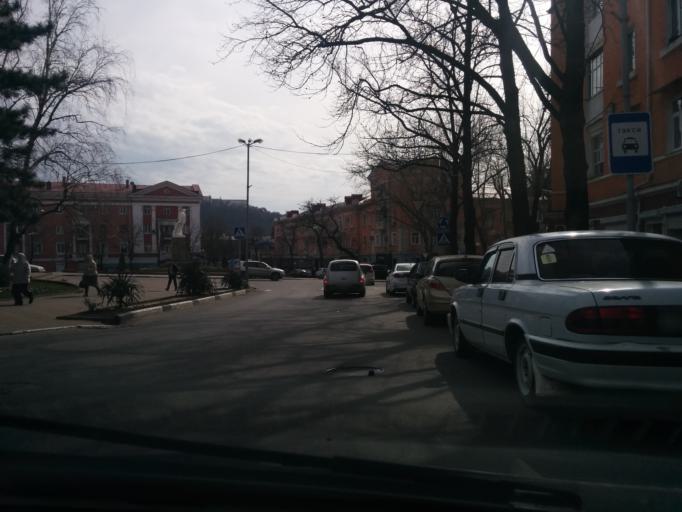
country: RU
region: Krasnodarskiy
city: Tuapse
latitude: 44.1000
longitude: 39.0788
